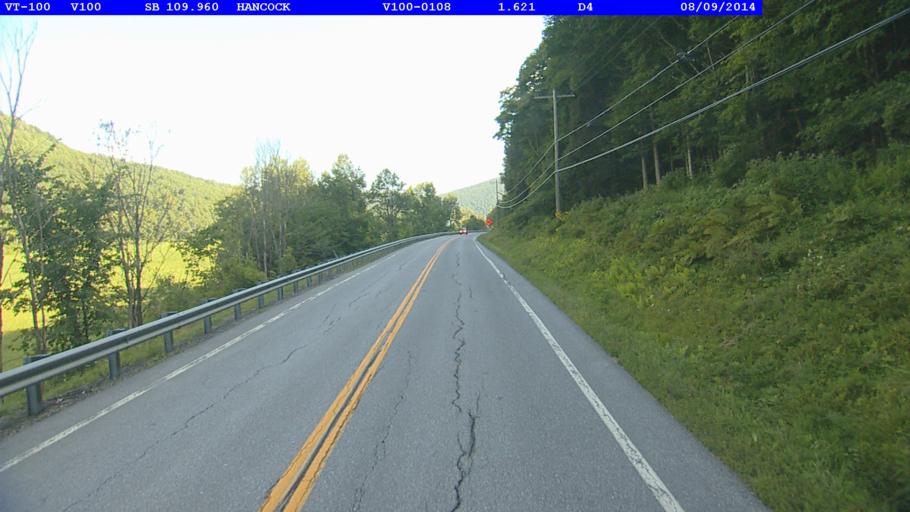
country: US
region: Vermont
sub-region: Orange County
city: Randolph
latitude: 43.9321
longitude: -72.8419
